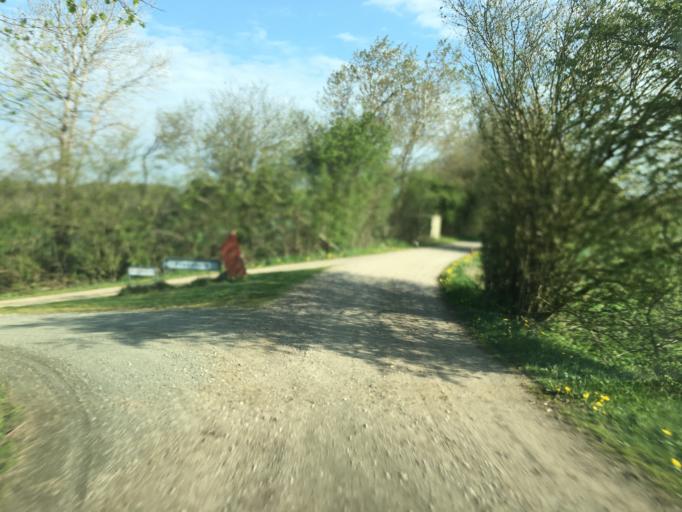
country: DK
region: South Denmark
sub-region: Haderslev Kommune
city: Vojens
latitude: 55.1788
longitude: 9.3869
